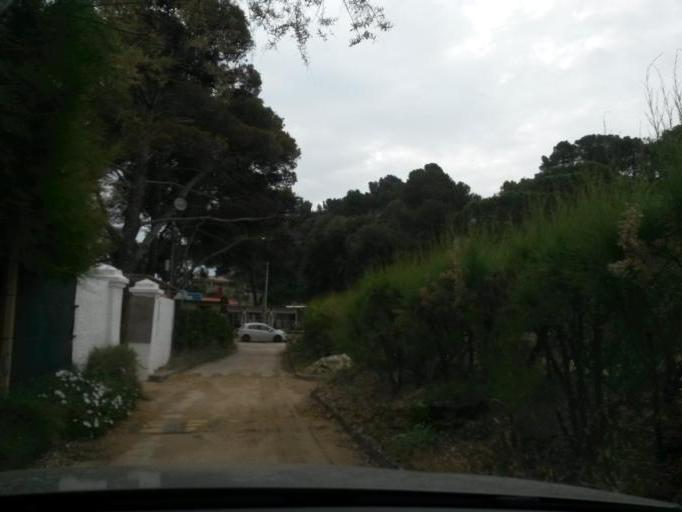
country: IT
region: Tuscany
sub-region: Provincia di Livorno
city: Capoliveri
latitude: 42.7598
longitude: 10.3574
